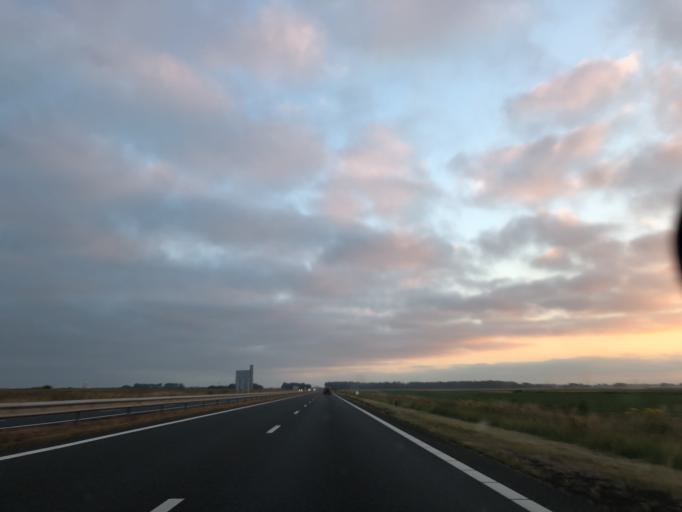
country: NL
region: Groningen
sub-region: Gemeente Veendam
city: Veendam
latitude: 53.1439
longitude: 6.8976
